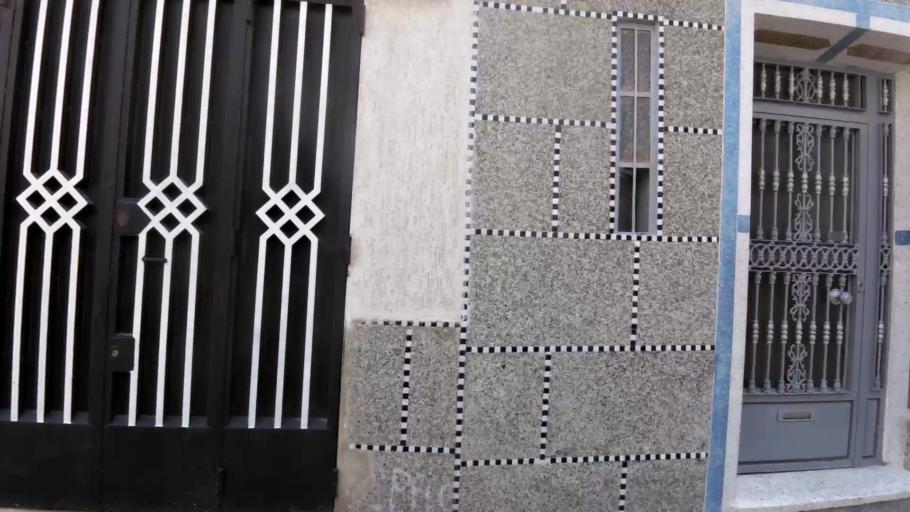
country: MA
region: Tanger-Tetouan
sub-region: Tanger-Assilah
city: Tangier
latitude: 35.7548
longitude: -5.8164
